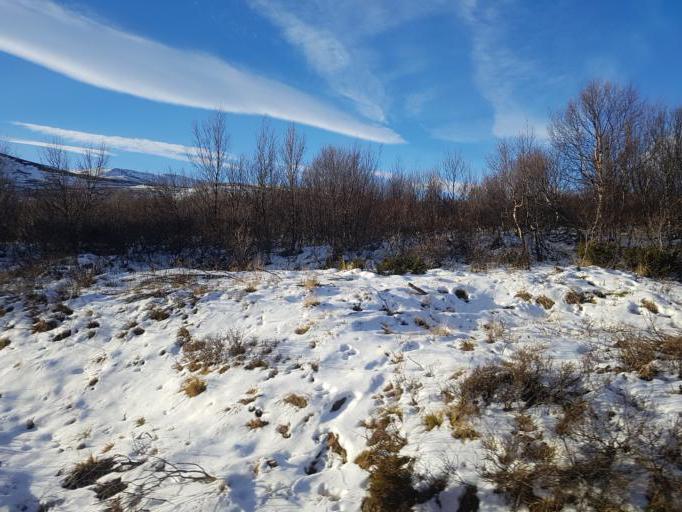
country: NO
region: Oppland
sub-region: Dovre
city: Dovre
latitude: 62.2253
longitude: 9.5374
